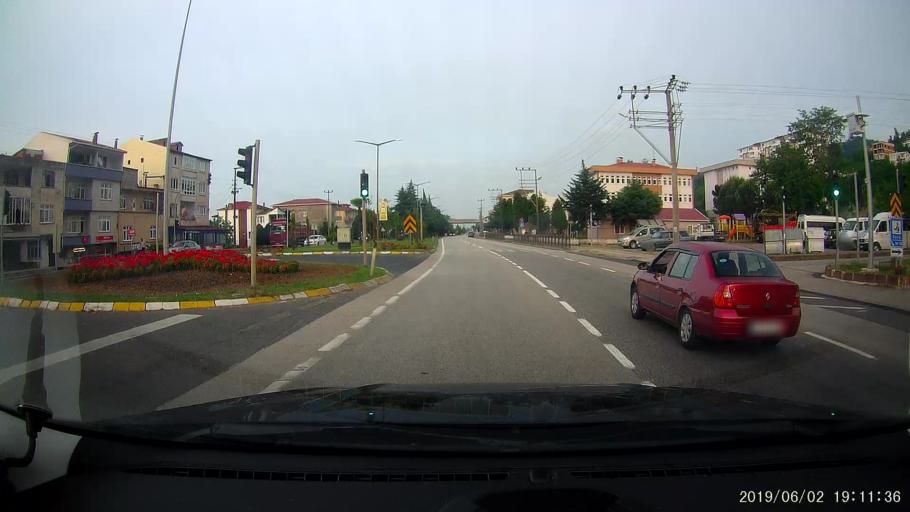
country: TR
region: Ordu
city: Gulyali
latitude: 40.9670
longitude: 38.0562
